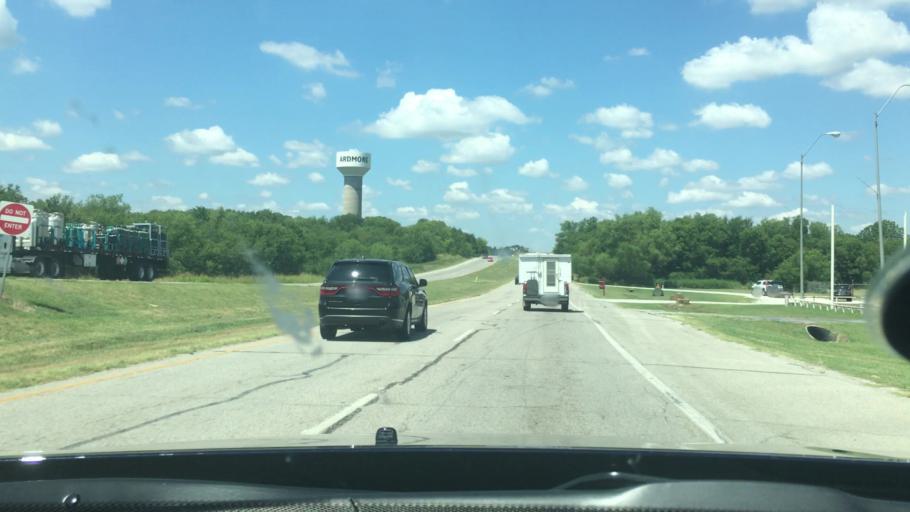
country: US
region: Oklahoma
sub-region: Carter County
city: Ardmore
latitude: 34.1730
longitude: -97.1935
